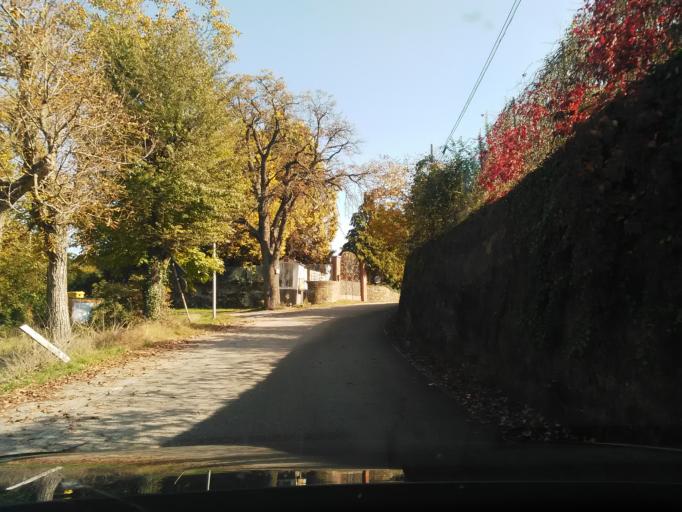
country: IT
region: Piedmont
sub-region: Provincia di Biella
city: Dorzano
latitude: 45.4267
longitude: 8.0835
